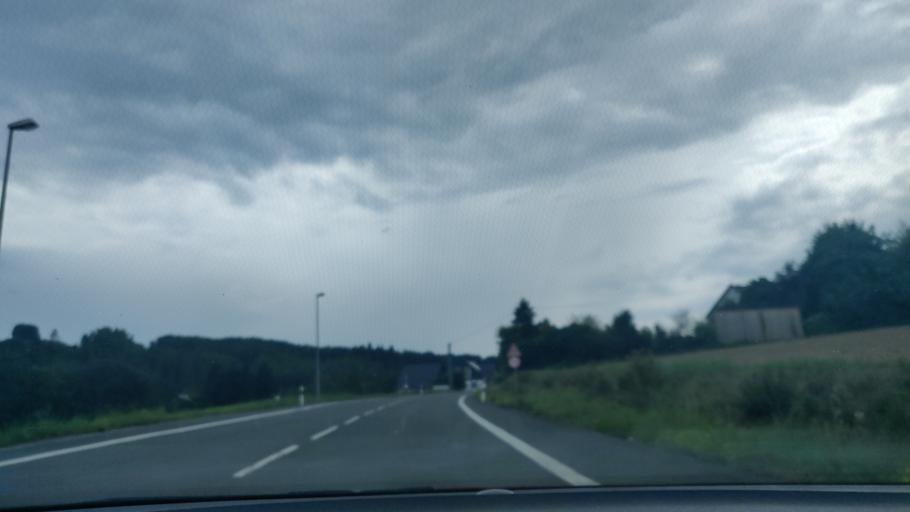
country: DE
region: North Rhine-Westphalia
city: Sprockhovel
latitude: 51.3613
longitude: 7.2595
